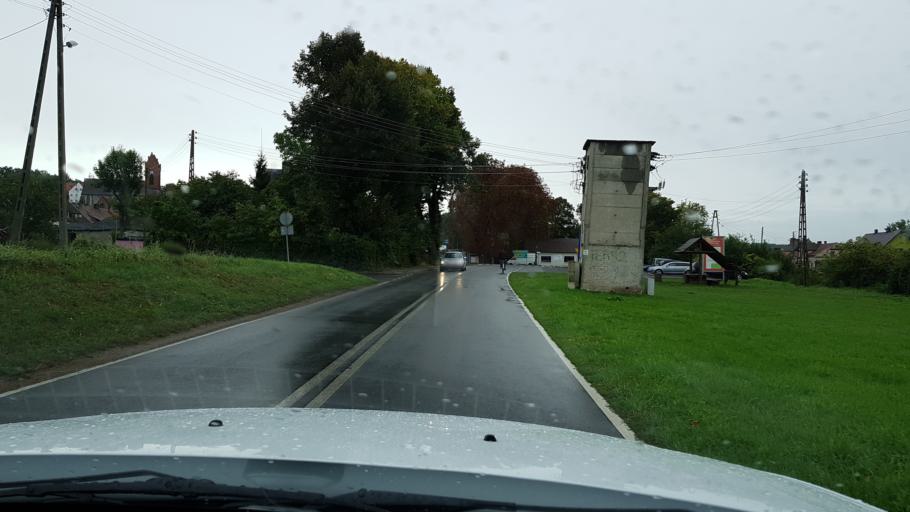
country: PL
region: West Pomeranian Voivodeship
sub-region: Powiat gryfinski
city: Cedynia
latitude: 52.8803
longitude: 14.2026
